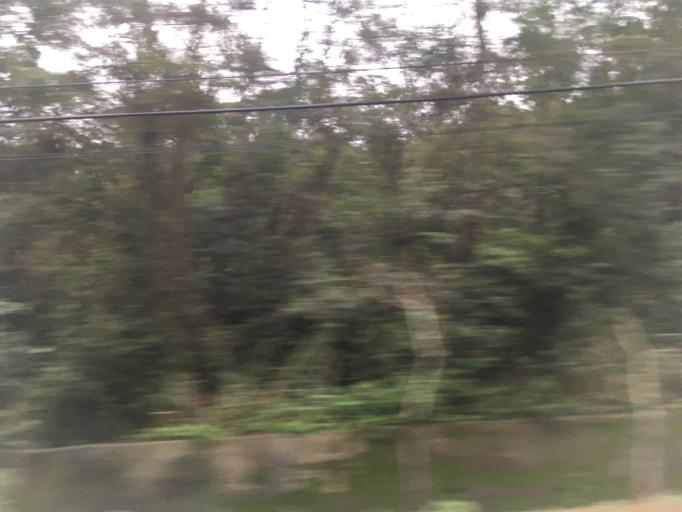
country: TW
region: Taiwan
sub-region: Miaoli
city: Miaoli
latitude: 24.4204
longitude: 120.7590
